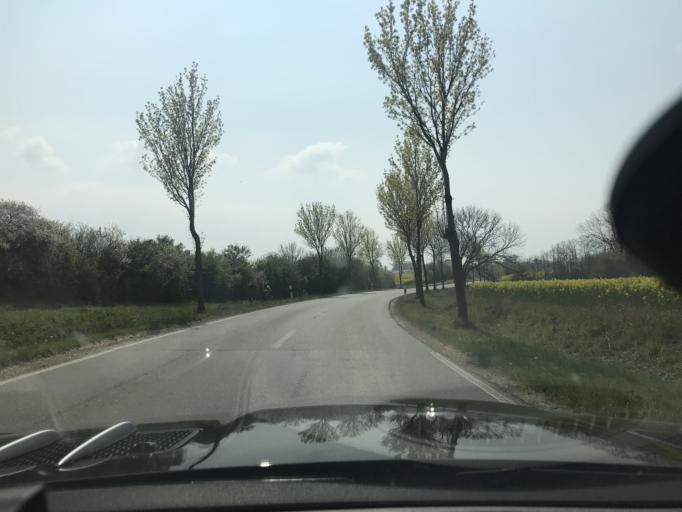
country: DE
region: Schleswig-Holstein
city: Gremersdorf
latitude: 54.3583
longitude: 10.9351
